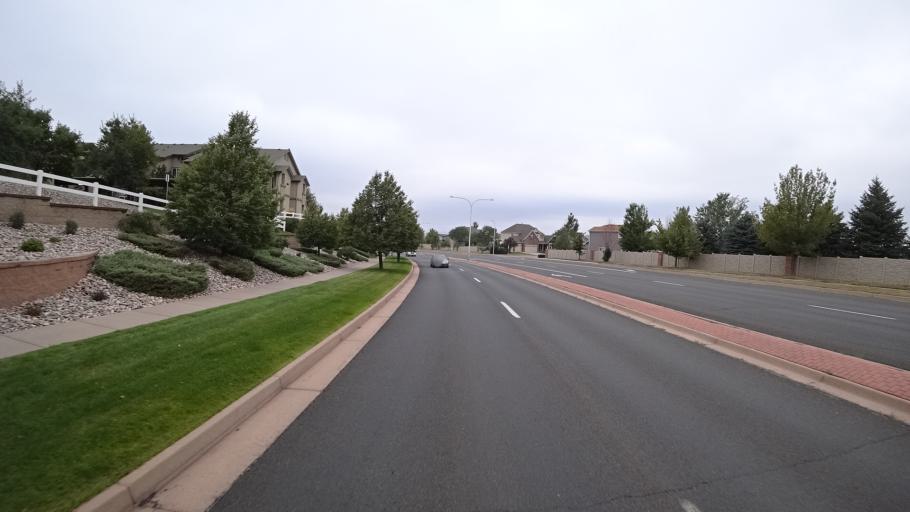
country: US
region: Colorado
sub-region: El Paso County
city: Cimarron Hills
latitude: 38.8961
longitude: -104.7008
